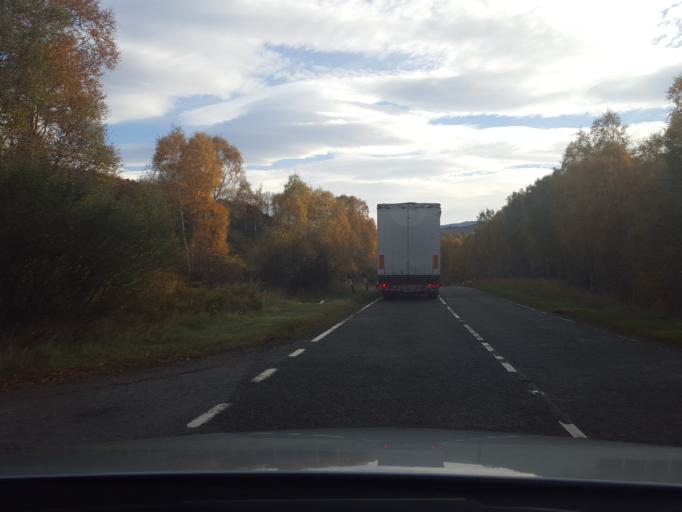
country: GB
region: Scotland
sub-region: Highland
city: Spean Bridge
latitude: 57.1454
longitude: -4.9868
